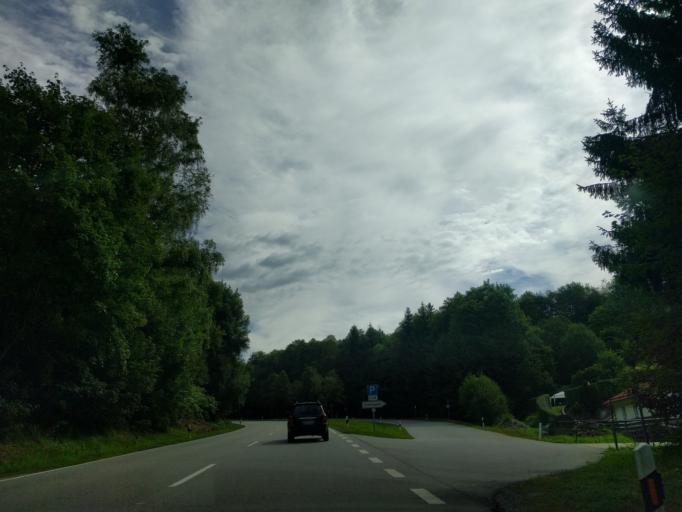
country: DE
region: Bavaria
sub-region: Lower Bavaria
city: Schaufling
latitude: 48.8640
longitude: 13.0296
